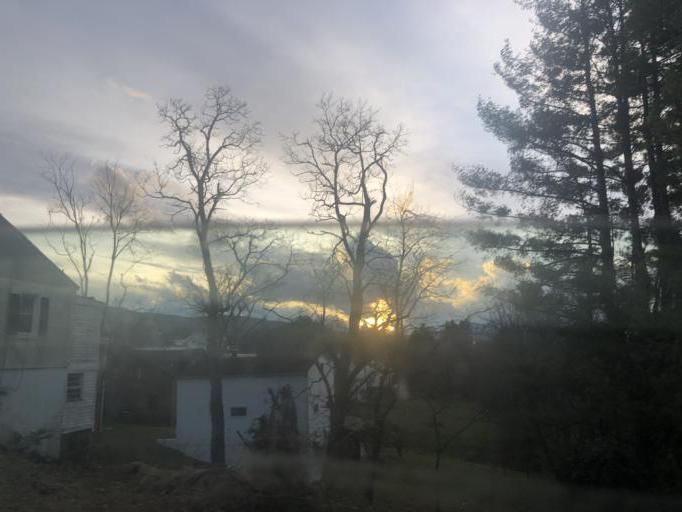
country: US
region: West Virginia
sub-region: Mercer County
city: Bluefield
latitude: 37.2514
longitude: -81.2196
